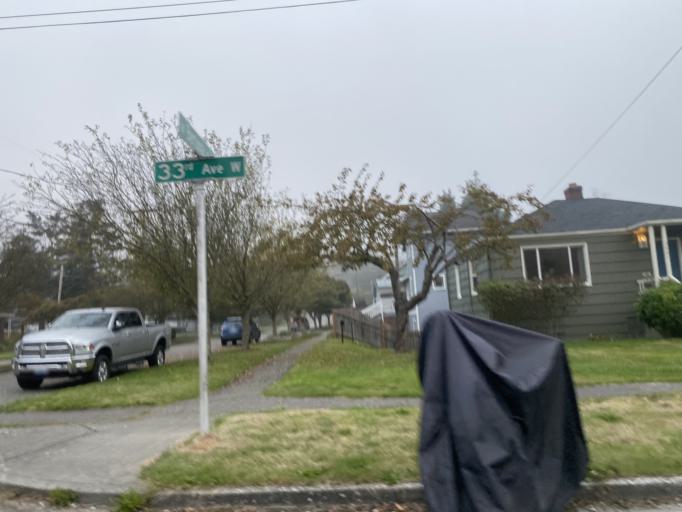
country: US
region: Washington
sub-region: King County
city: Seattle
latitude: 47.6505
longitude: -122.3995
